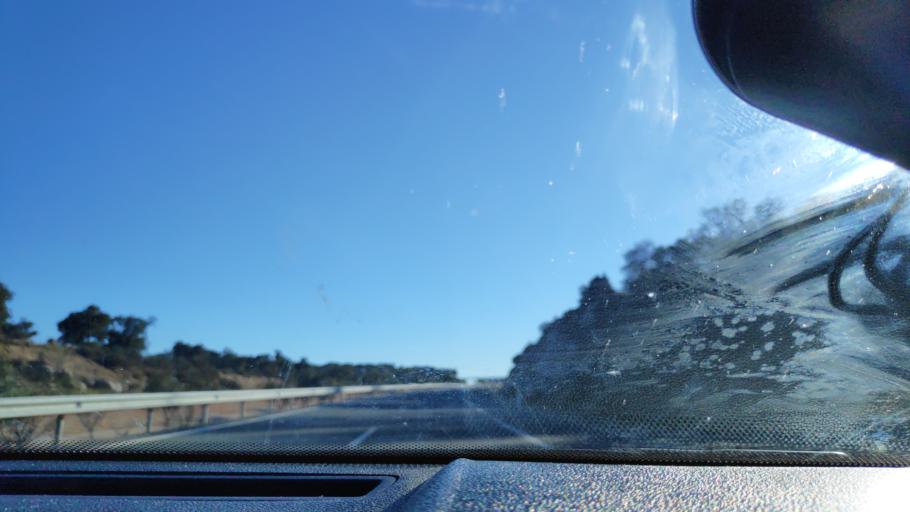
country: ES
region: Andalusia
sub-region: Provincia de Huelva
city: Santa Olalla del Cala
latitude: 37.9367
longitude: -6.2267
